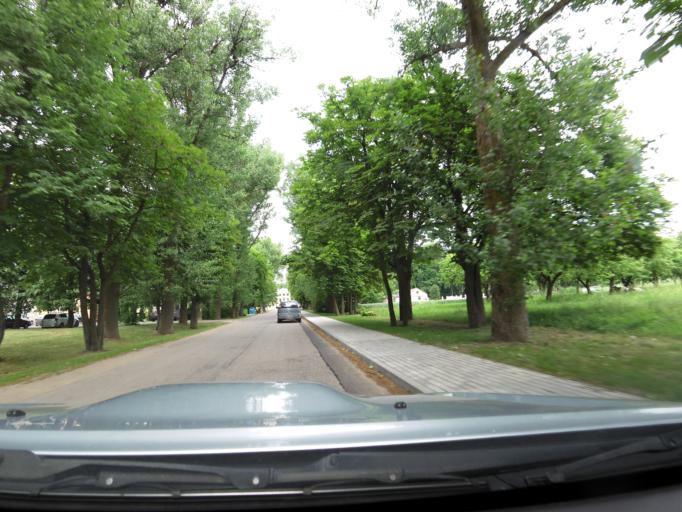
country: LT
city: Vilkaviskis
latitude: 54.6373
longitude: 22.9774
